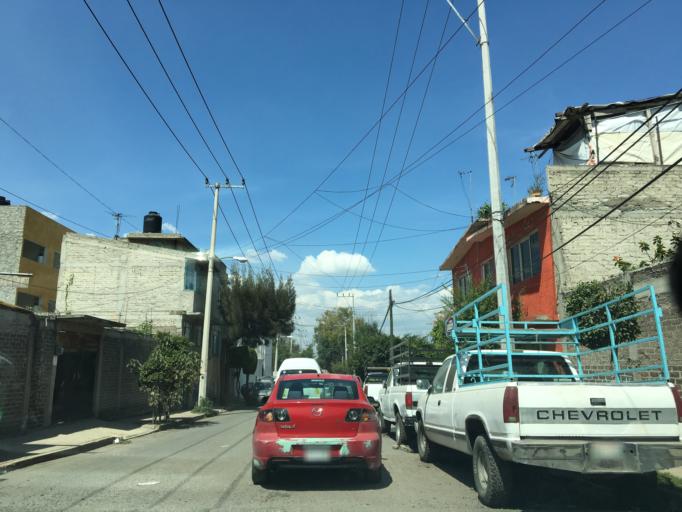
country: MX
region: Mexico
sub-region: La Paz
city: Emiliano Zapata
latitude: 19.3507
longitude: -98.9830
